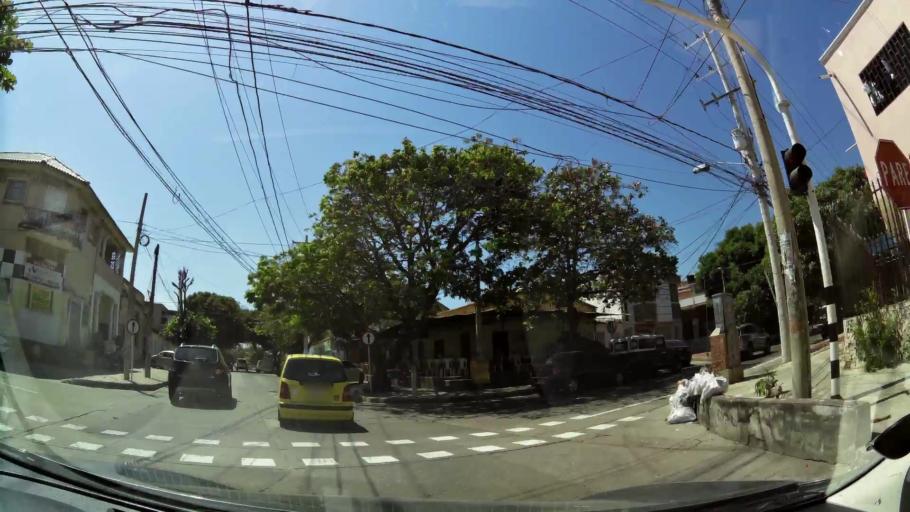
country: CO
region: Atlantico
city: Barranquilla
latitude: 10.9915
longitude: -74.7946
